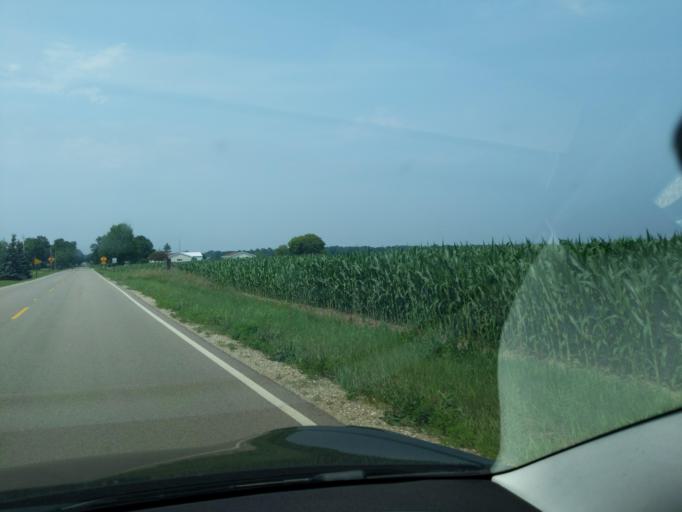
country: US
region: Michigan
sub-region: Clinton County
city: Saint Johns
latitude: 42.9259
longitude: -84.5822
